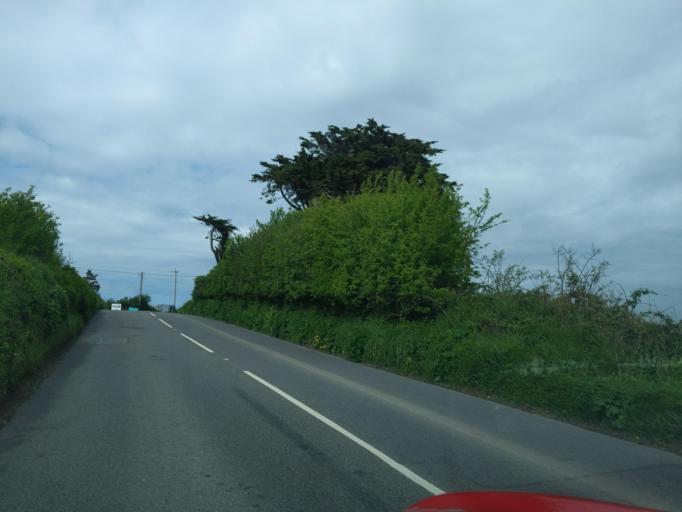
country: GB
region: England
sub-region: Cornwall
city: Wadebridge
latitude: 50.5501
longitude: -4.8638
